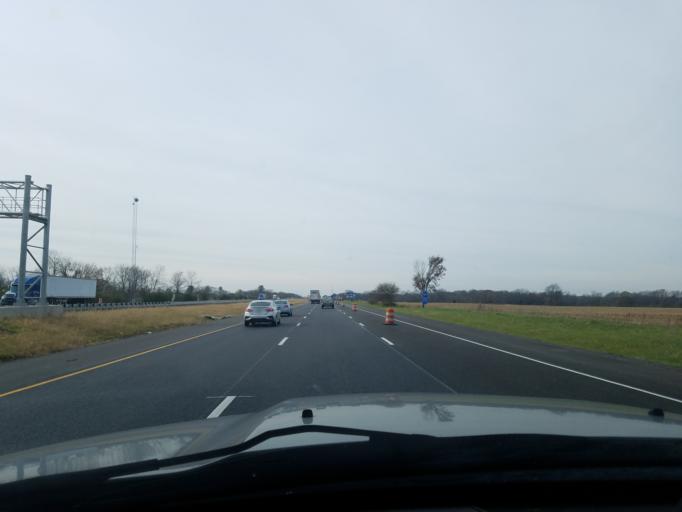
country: US
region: Indiana
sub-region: Hancock County
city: Fortville
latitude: 39.9915
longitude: -85.8812
